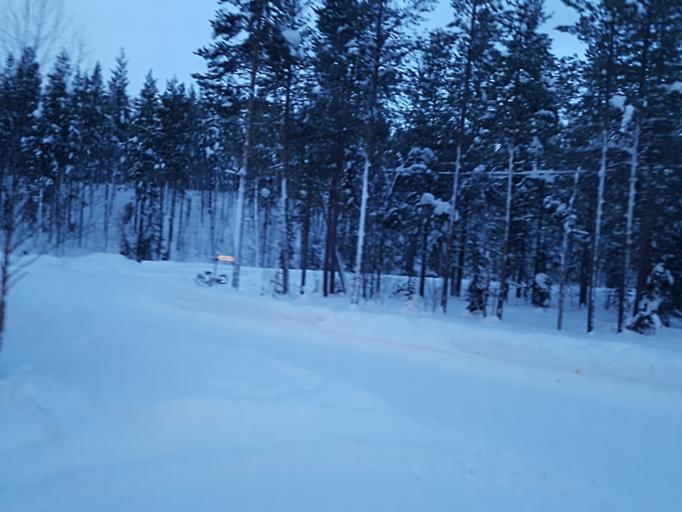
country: FI
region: Lapland
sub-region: Tunturi-Lappi
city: Kolari
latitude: 67.6160
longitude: 24.1244
